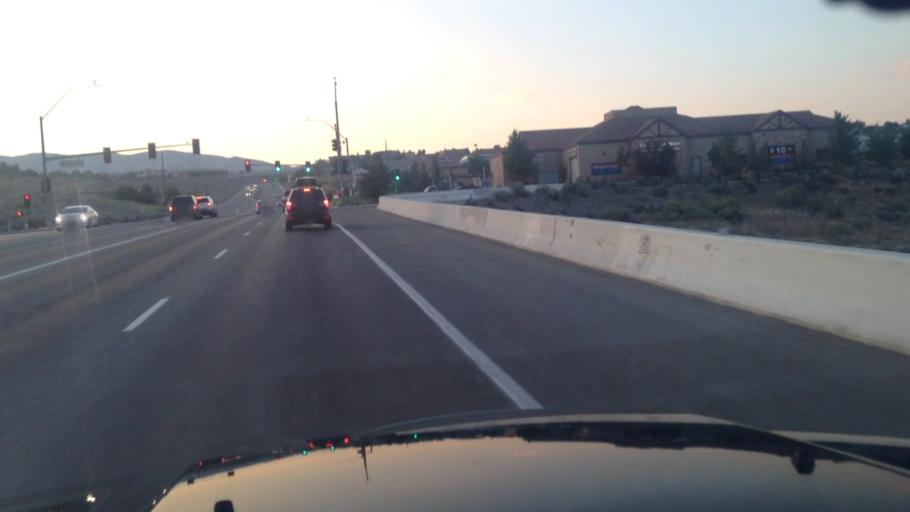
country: US
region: Nevada
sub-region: Washoe County
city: Reno
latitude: 39.5117
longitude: -119.8588
